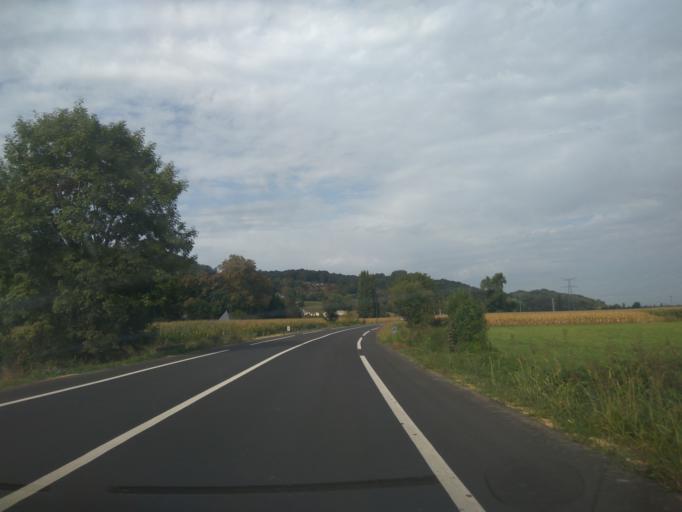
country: FR
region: Aquitaine
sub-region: Departement des Pyrenees-Atlantiques
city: Arbus
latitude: 43.3381
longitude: -0.5060
